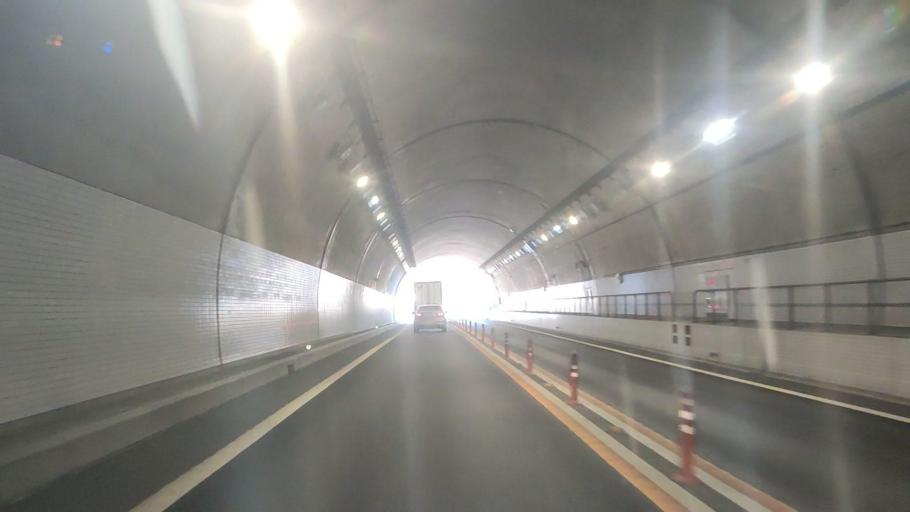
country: JP
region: Fukuoka
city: Kanda
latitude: 33.7683
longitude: 130.9655
